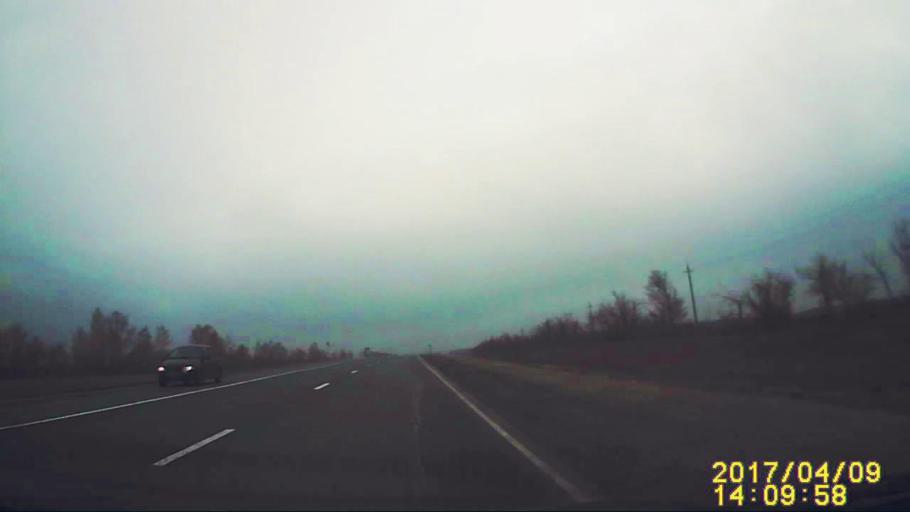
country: RU
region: Ulyanovsk
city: Krasnyy Gulyay
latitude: 54.0335
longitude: 48.2131
